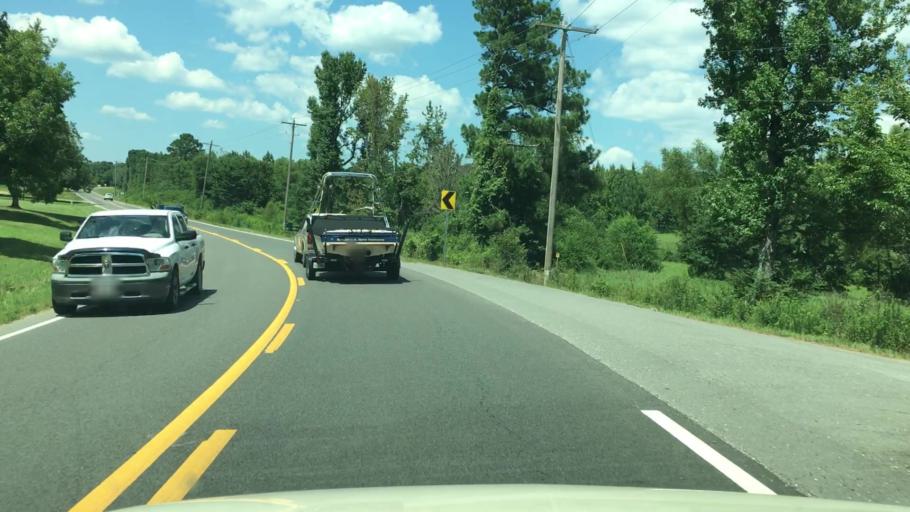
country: US
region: Arkansas
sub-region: Garland County
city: Lake Hamilton
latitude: 34.2948
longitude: -93.1624
